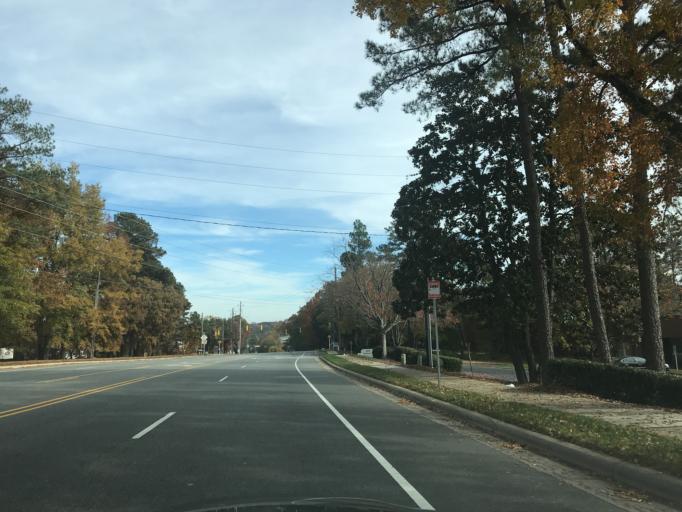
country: US
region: North Carolina
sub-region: Wake County
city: West Raleigh
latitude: 35.8154
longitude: -78.7019
